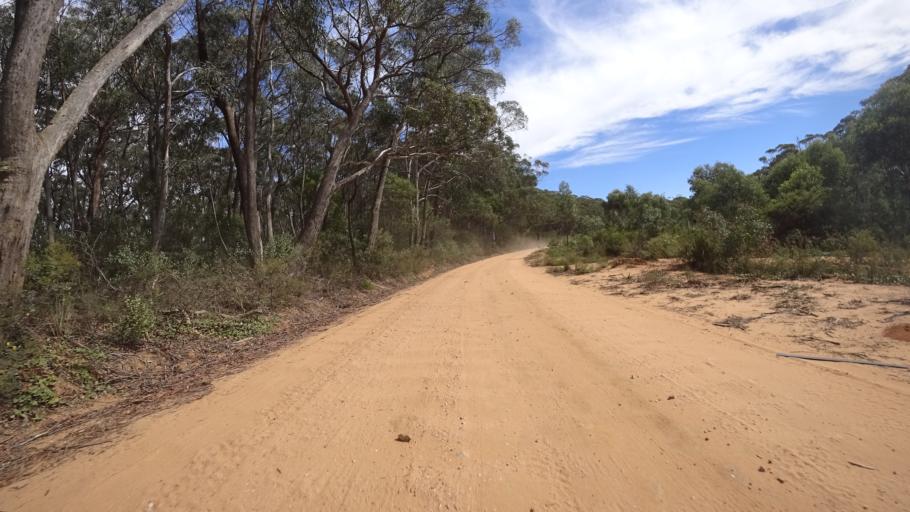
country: AU
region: New South Wales
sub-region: Lithgow
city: Lithgow
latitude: -33.3229
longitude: 150.2458
